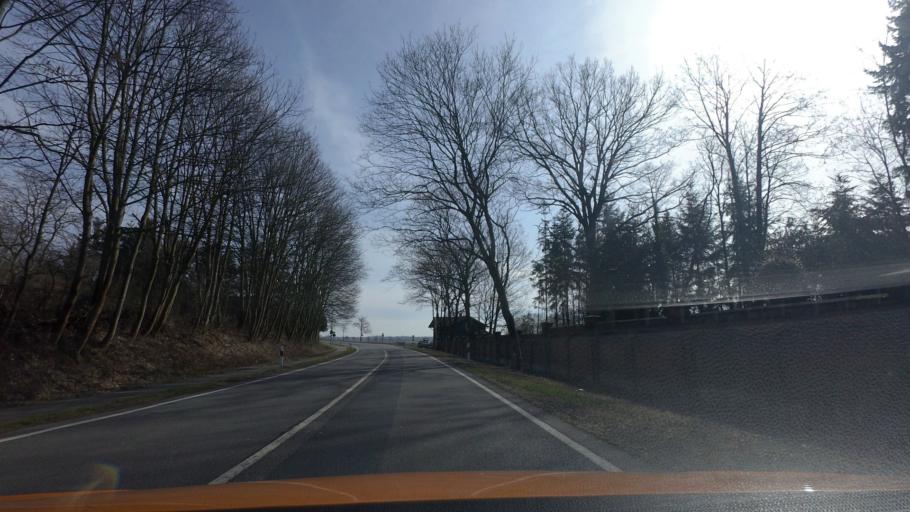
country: DE
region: Lower Saxony
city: Gehrden
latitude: 52.3307
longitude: 9.6109
